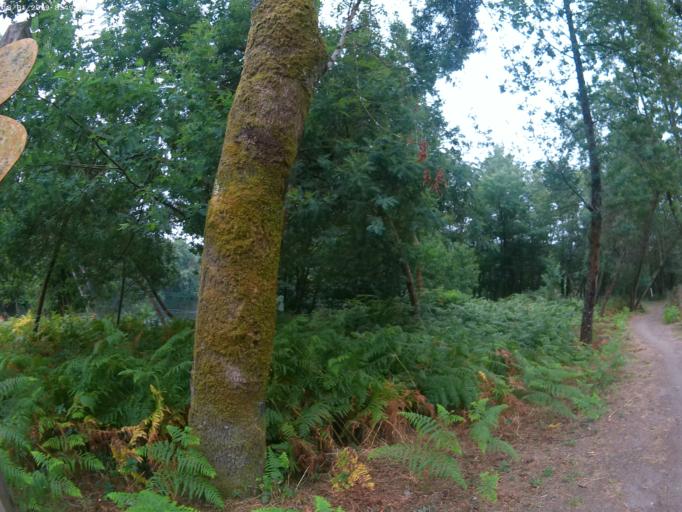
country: PT
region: Viana do Castelo
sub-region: Ponte da Barca
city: Ponte da Barca
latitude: 41.8072
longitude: -8.4318
